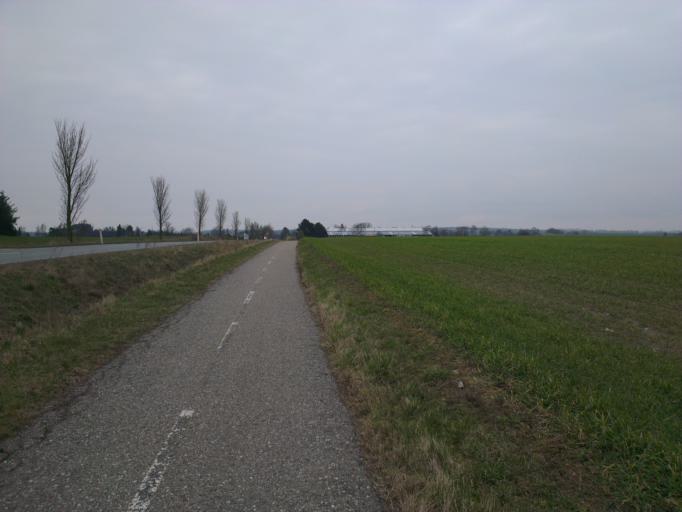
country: DK
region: Capital Region
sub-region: Frederikssund Kommune
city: Jaegerspris
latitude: 55.8202
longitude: 11.9847
